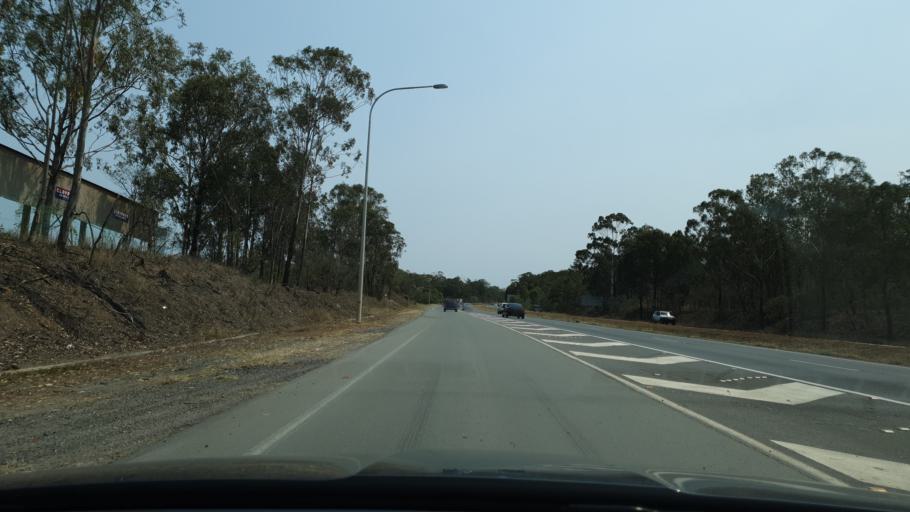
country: AU
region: Queensland
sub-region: Ipswich
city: Bundamba
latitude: -27.6057
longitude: 152.8306
